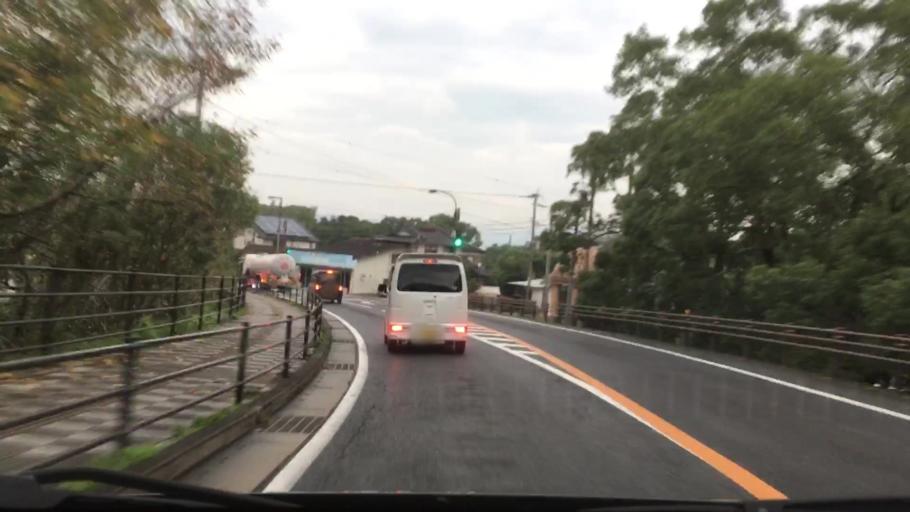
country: JP
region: Nagasaki
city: Sasebo
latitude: 33.0556
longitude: 129.7610
